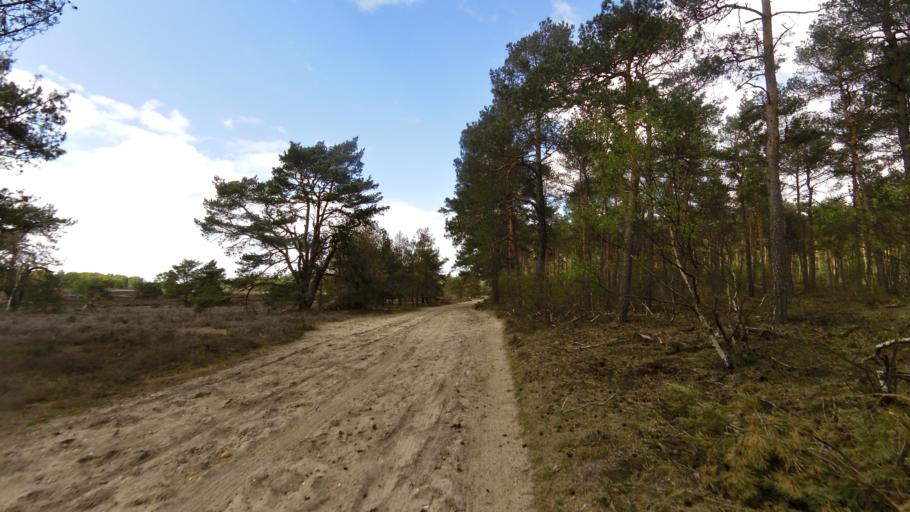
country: NL
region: Gelderland
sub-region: Gemeente Apeldoorn
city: Loenen
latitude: 52.0792
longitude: 6.0113
